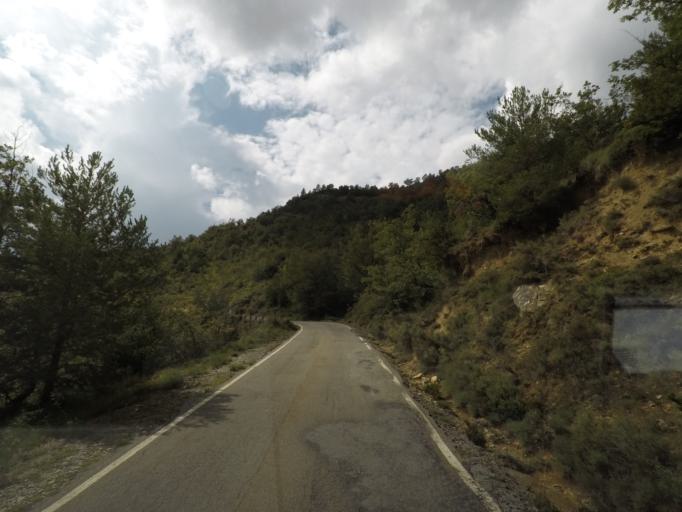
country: ES
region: Aragon
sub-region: Provincia de Huesca
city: Boltana
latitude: 42.4072
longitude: -0.0067
